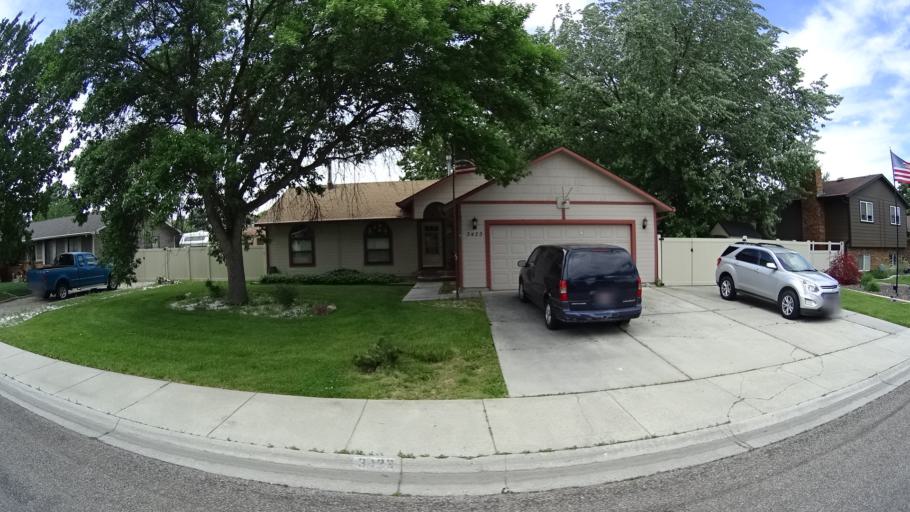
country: US
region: Idaho
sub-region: Ada County
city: Eagle
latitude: 43.6358
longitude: -116.3244
